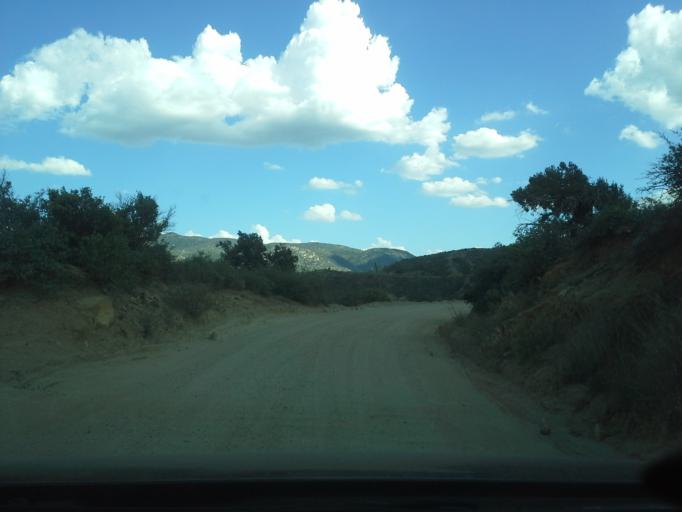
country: US
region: Arizona
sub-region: Yavapai County
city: Mayer
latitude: 34.2222
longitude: -112.3116
